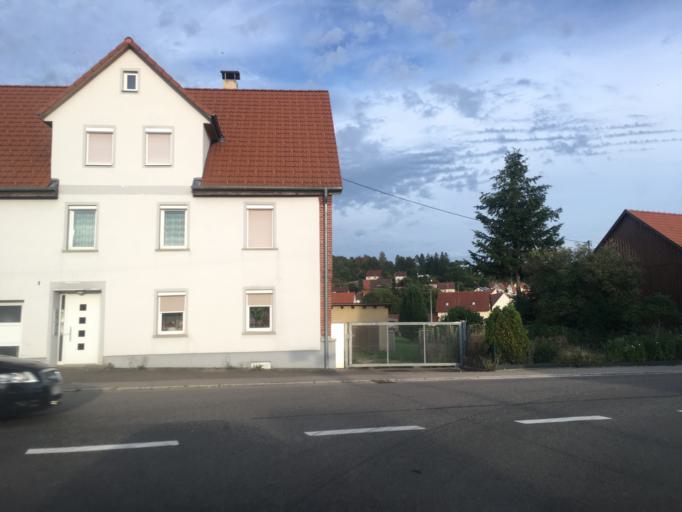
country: DE
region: Baden-Wuerttemberg
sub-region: Tuebingen Region
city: Gomadingen
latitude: 48.4314
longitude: 9.3775
